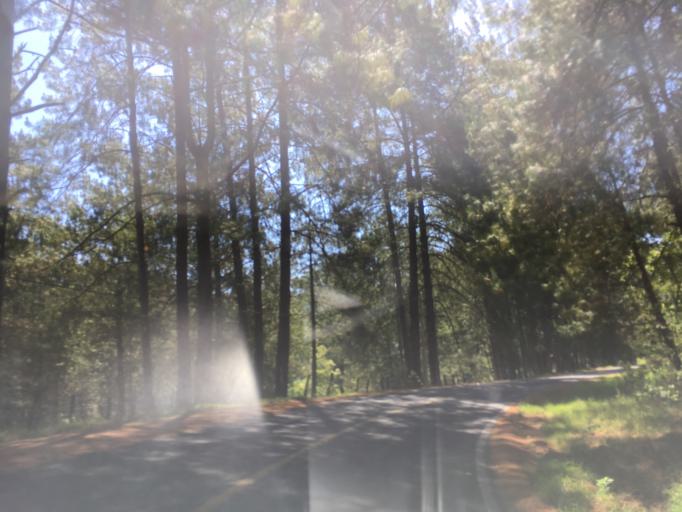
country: MX
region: Michoacan
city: Tzitzio
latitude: 19.6586
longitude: -100.8013
